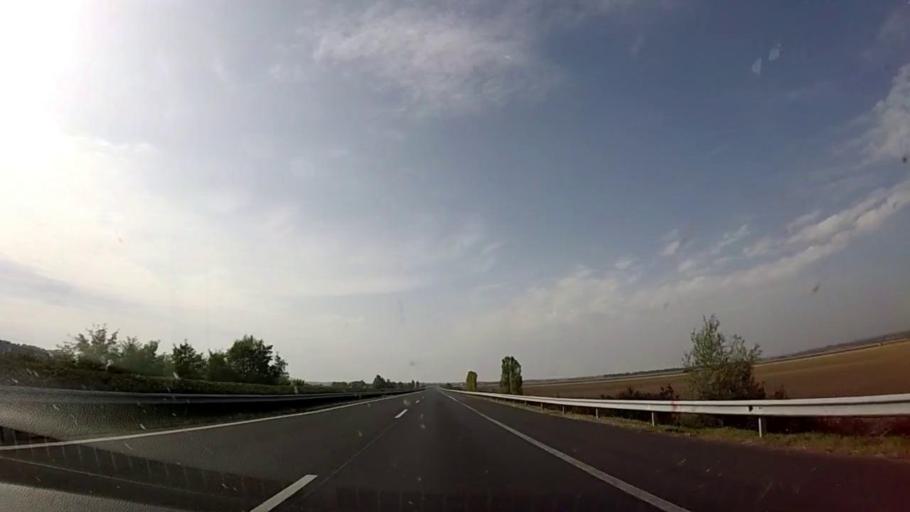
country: HU
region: Zala
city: Becsehely
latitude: 46.4319
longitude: 16.7916
